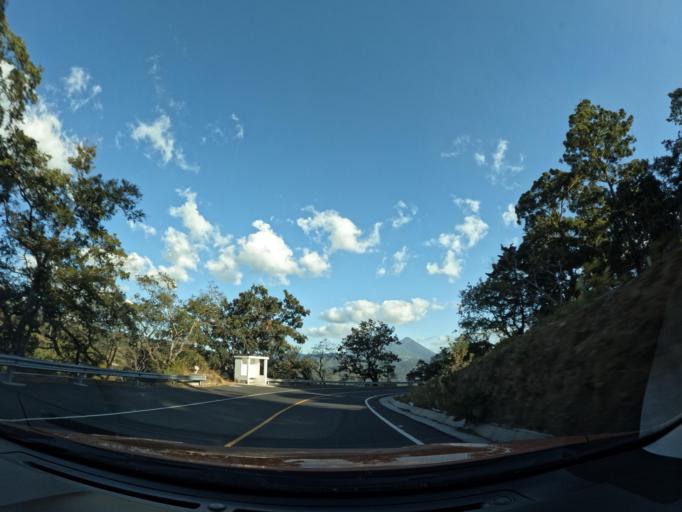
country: GT
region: Escuintla
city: Palin
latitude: 14.4432
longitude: -90.6940
